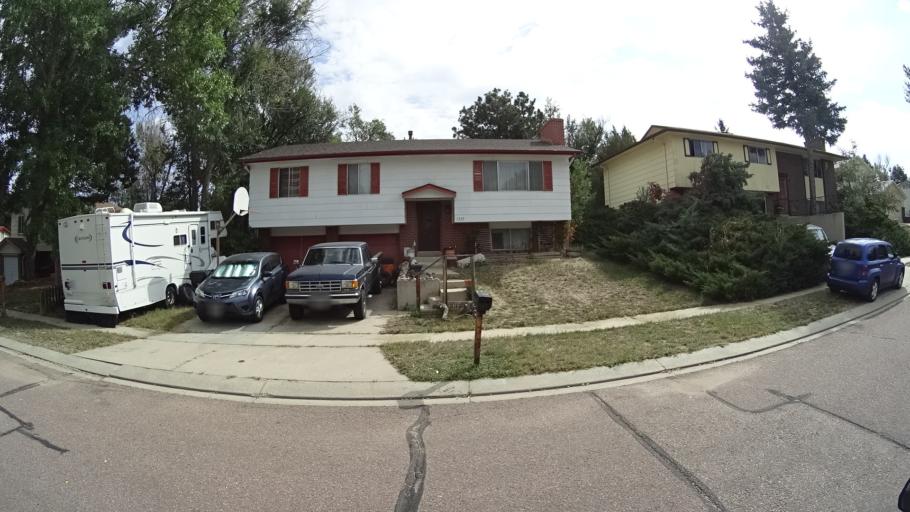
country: US
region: Colorado
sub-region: El Paso County
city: Cimarron Hills
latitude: 38.8603
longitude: -104.7299
